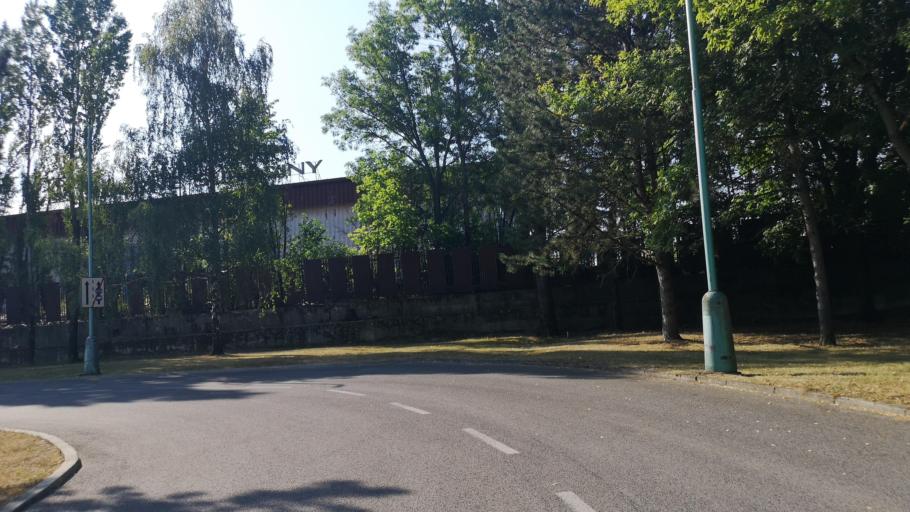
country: SK
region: Nitriansky
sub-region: Okres Nitra
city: Nitra
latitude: 48.3152
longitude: 18.0433
